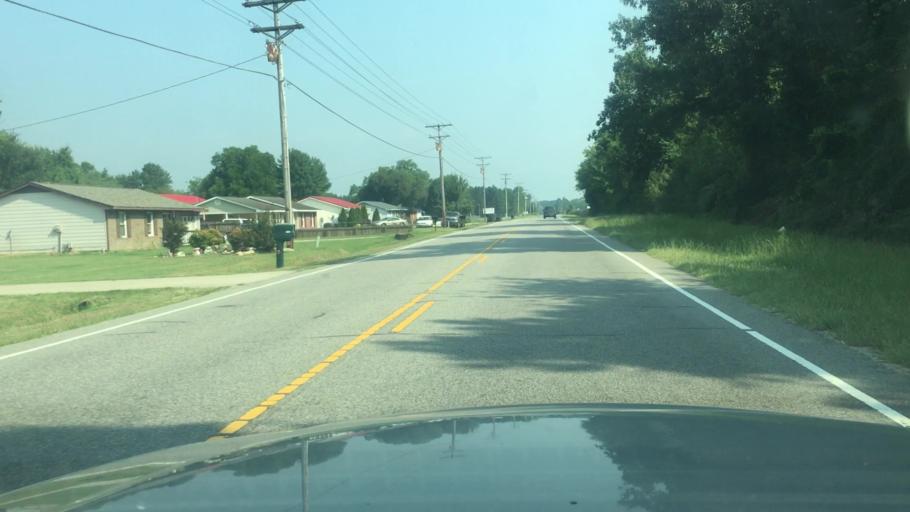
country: US
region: North Carolina
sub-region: Cumberland County
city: Hope Mills
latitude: 34.8995
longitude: -78.9003
